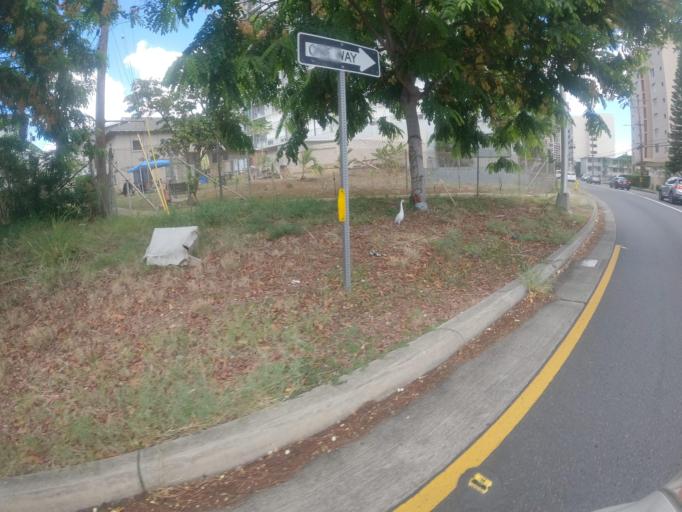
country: US
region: Hawaii
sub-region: Honolulu County
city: Honolulu
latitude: 21.3054
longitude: -157.8507
